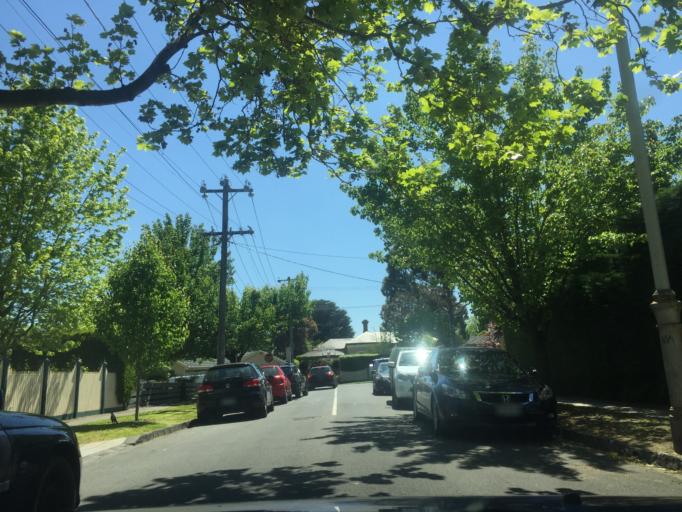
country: AU
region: Victoria
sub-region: Boroondara
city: Canterbury
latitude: -37.8179
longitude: 145.0889
